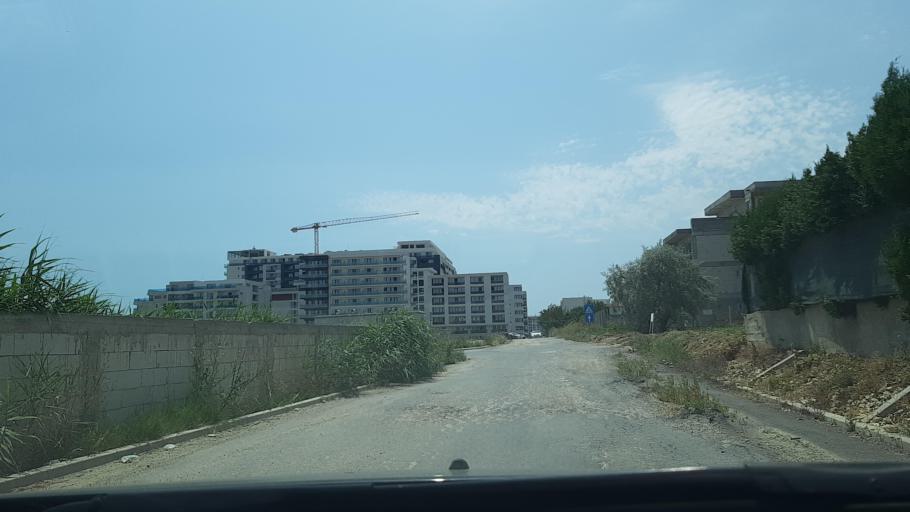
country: RO
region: Constanta
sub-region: Comuna Navodari
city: Navodari
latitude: 44.2972
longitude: 28.6232
